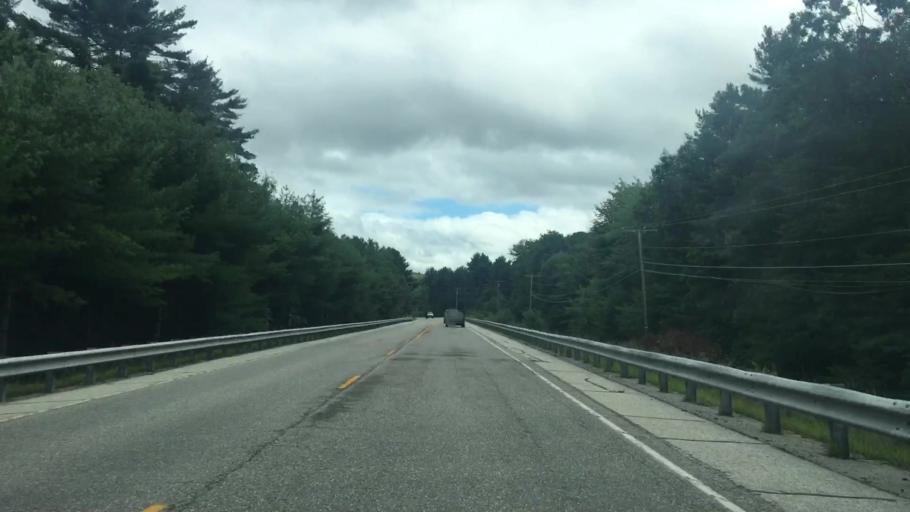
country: US
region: Maine
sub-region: York County
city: Lake Arrowhead
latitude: 43.6258
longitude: -70.7407
